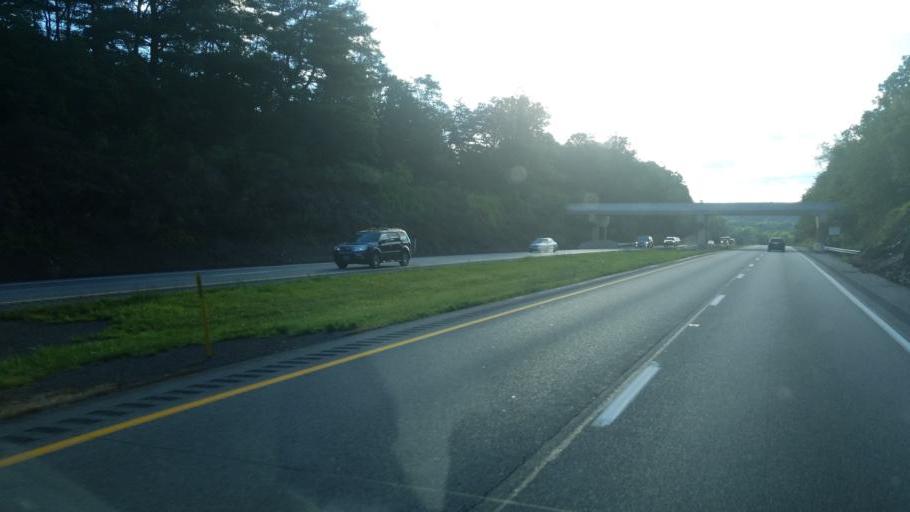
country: US
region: Maryland
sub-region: Washington County
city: Hancock
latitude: 39.7948
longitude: -78.2245
